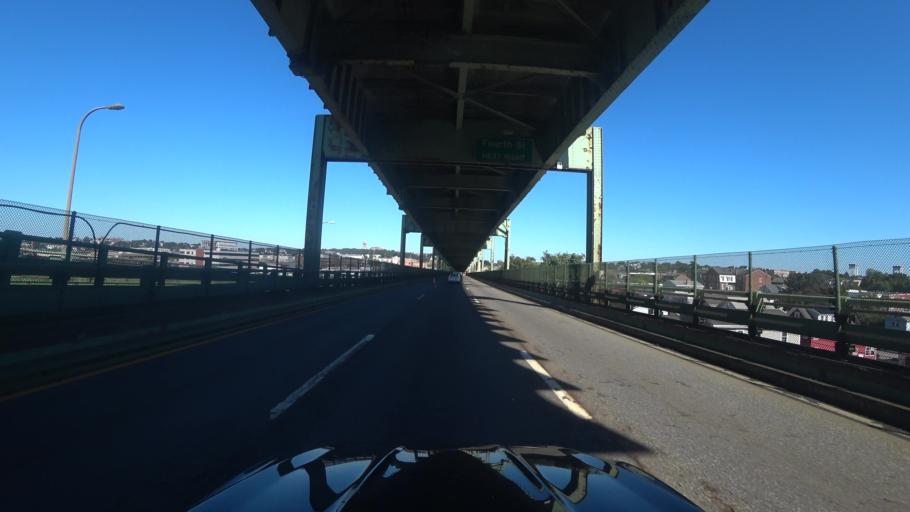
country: US
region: Massachusetts
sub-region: Suffolk County
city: Chelsea
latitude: 42.3885
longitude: -71.0433
